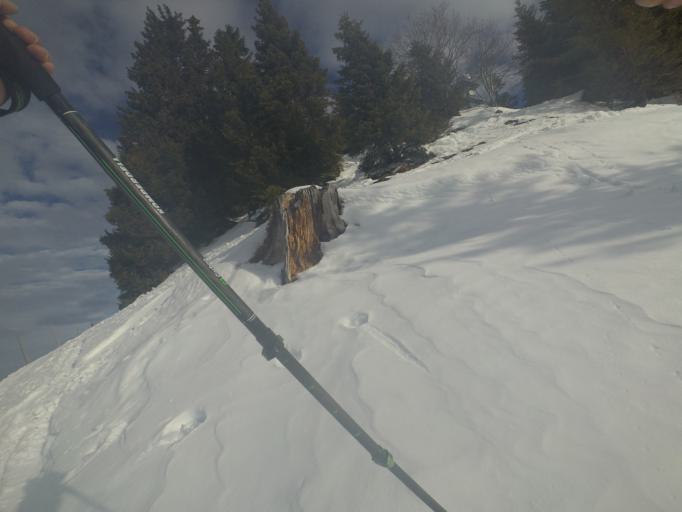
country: AT
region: Salzburg
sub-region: Politischer Bezirk Sankt Johann im Pongau
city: Sankt Johann im Pongau
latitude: 47.3077
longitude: 13.2335
